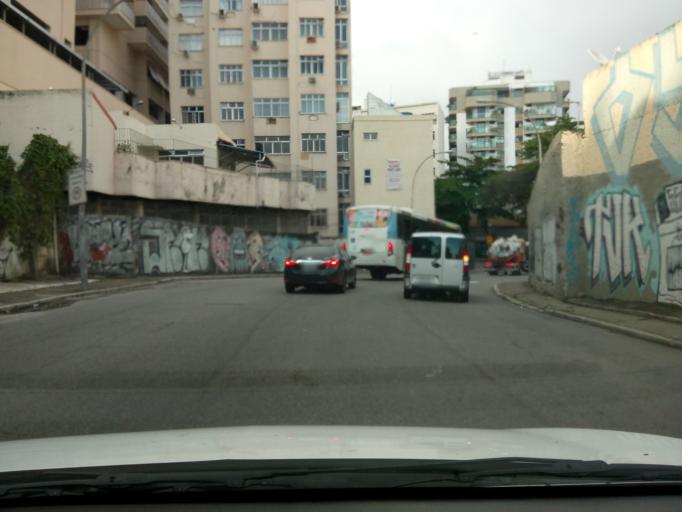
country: BR
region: Rio de Janeiro
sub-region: Rio De Janeiro
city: Rio de Janeiro
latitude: -22.9520
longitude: -43.1814
